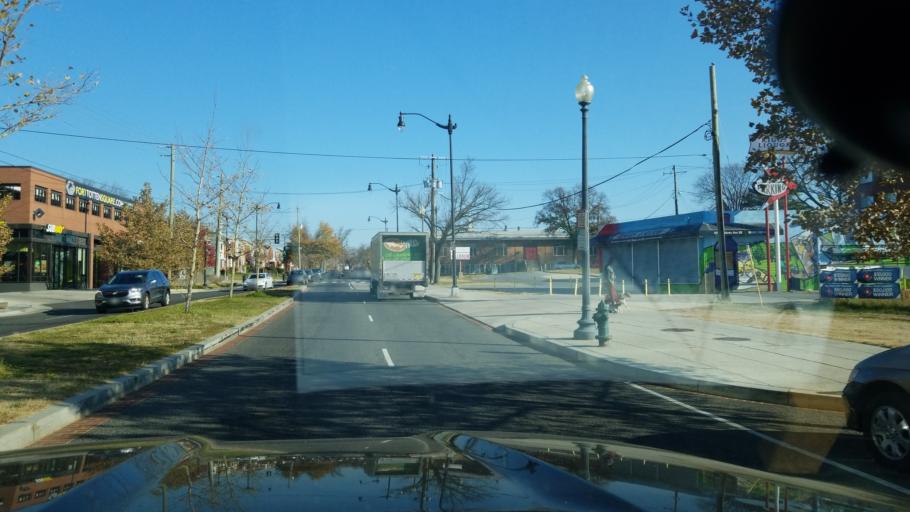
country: US
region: Maryland
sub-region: Prince George's County
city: Chillum
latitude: 38.9580
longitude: -77.0016
